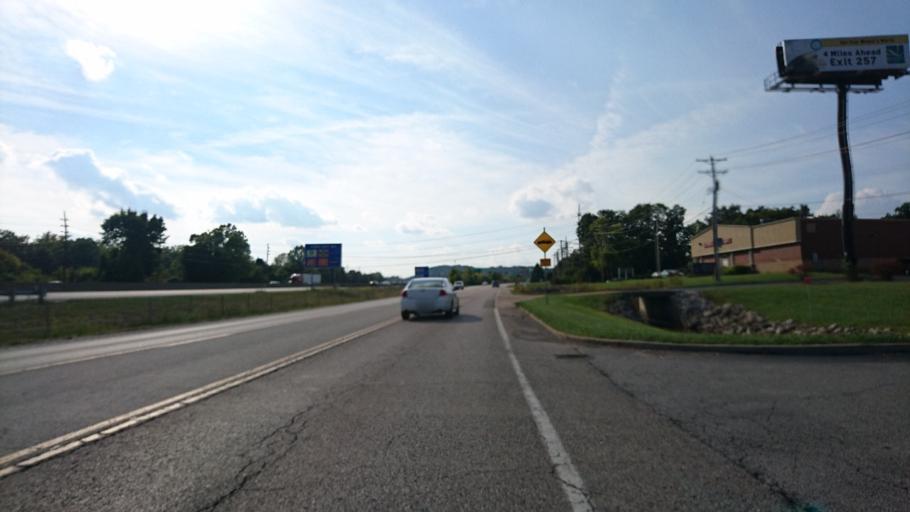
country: US
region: Missouri
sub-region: Saint Louis County
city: Eureka
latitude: 38.5047
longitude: -90.6657
